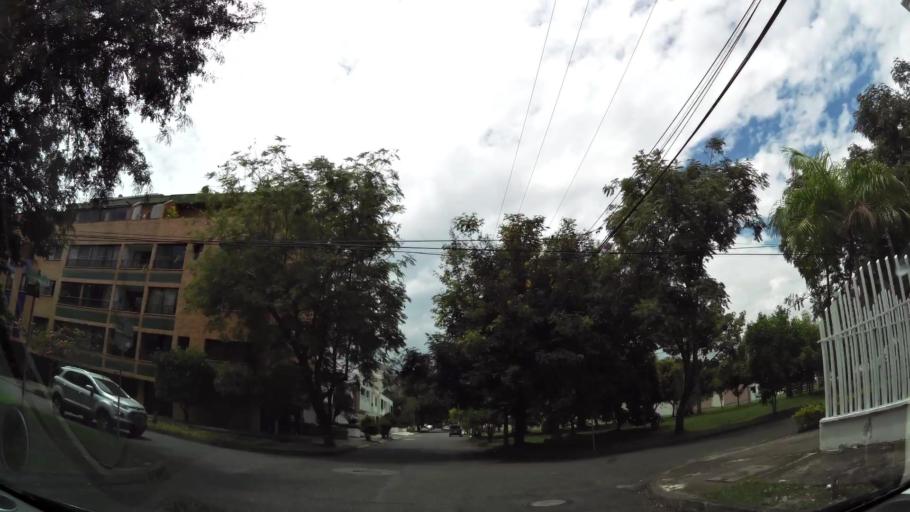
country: CO
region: Valle del Cauca
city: Cali
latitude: 3.3842
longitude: -76.5304
